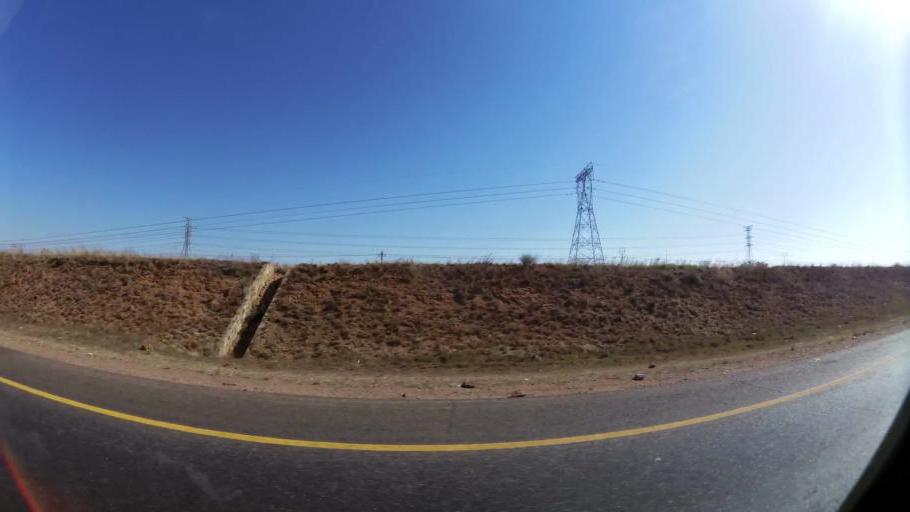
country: ZA
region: Gauteng
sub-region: City of Tshwane Metropolitan Municipality
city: Mabopane
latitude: -25.5457
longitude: 28.1108
